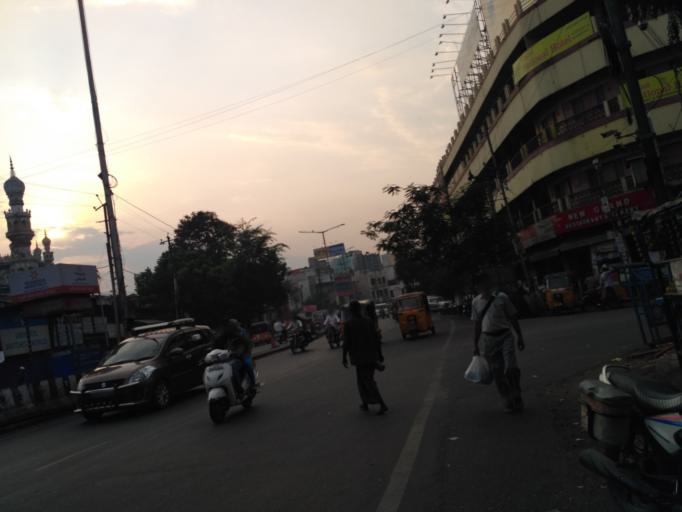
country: IN
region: Telangana
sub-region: Hyderabad
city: Hyderabad
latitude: 17.3743
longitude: 78.4763
